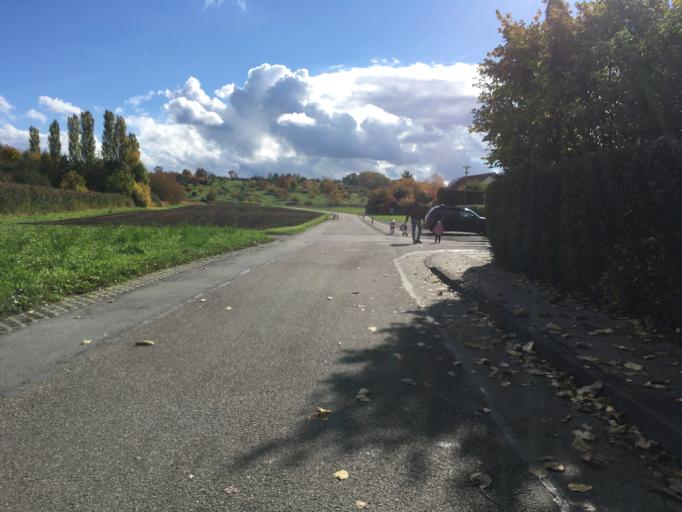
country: DE
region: Baden-Wuerttemberg
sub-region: Regierungsbezirk Stuttgart
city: Pfedelbach
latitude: 49.1776
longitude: 9.5094
